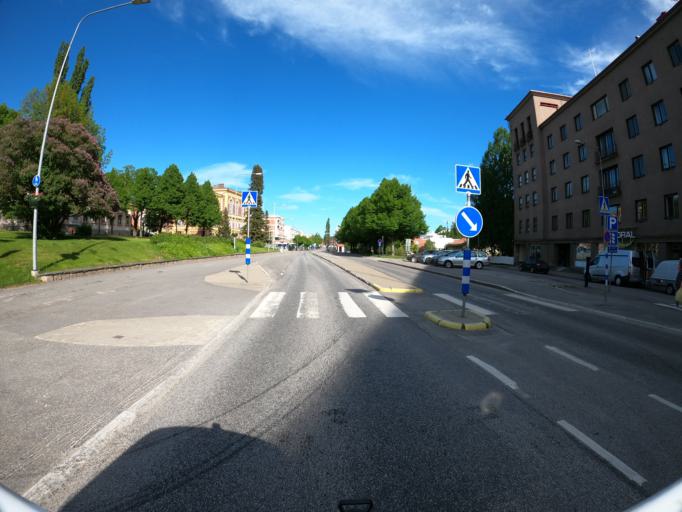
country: FI
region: Southern Savonia
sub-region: Savonlinna
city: Savonlinna
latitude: 61.8672
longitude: 28.8902
